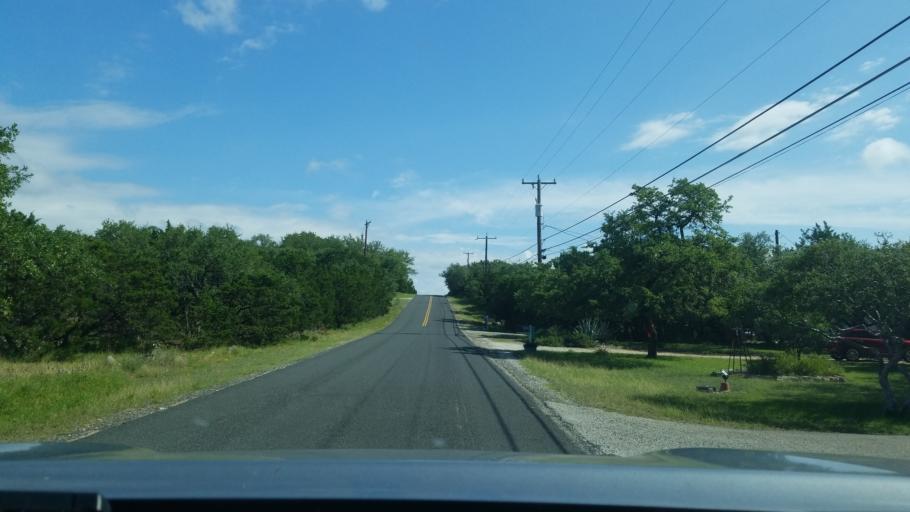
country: US
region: Texas
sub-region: Comal County
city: Bulverde
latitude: 29.7458
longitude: -98.4427
